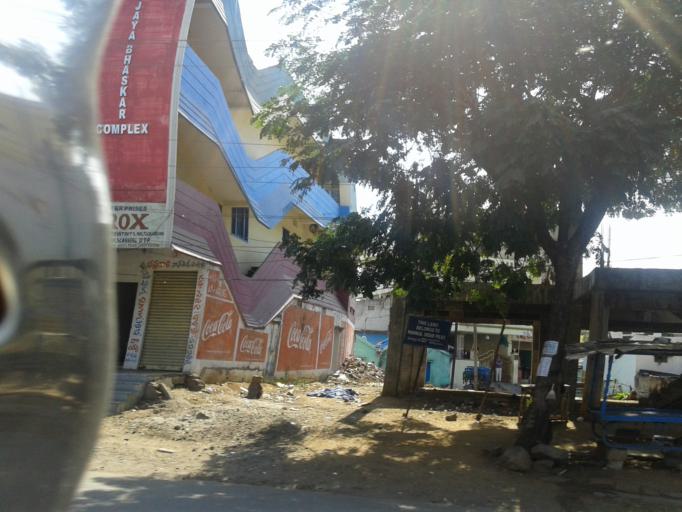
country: IN
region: Telangana
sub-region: Warangal
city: Warangal
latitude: 17.9974
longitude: 79.5883
